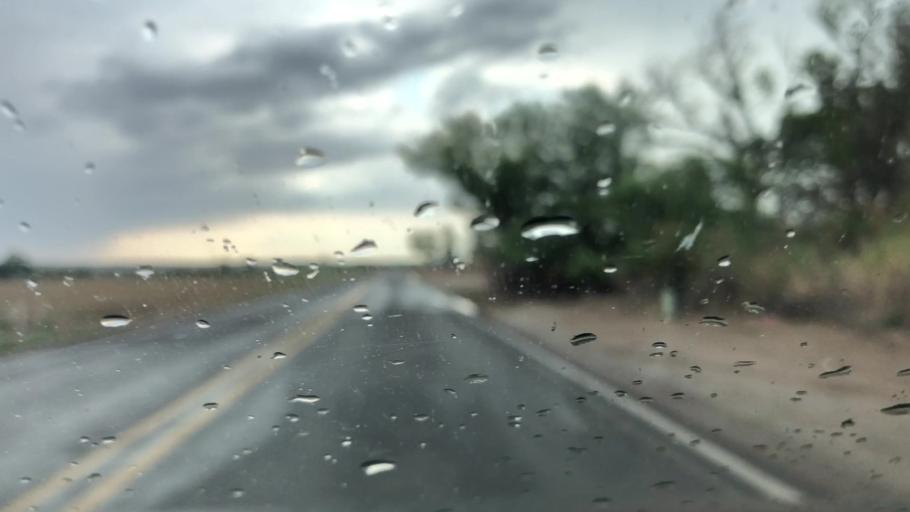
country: US
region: New Mexico
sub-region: Dona Ana County
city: Vado
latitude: 32.0689
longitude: -106.6806
